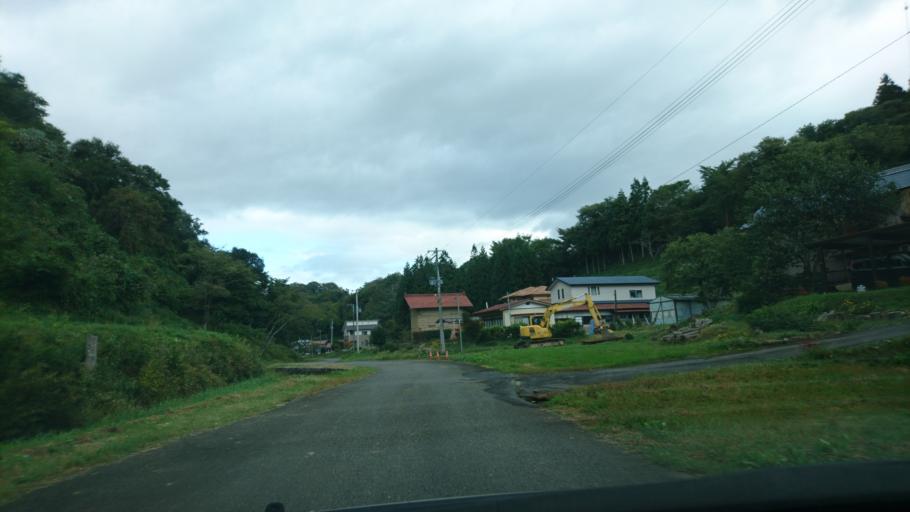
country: JP
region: Iwate
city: Ichinoseki
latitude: 38.8944
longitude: 141.0902
